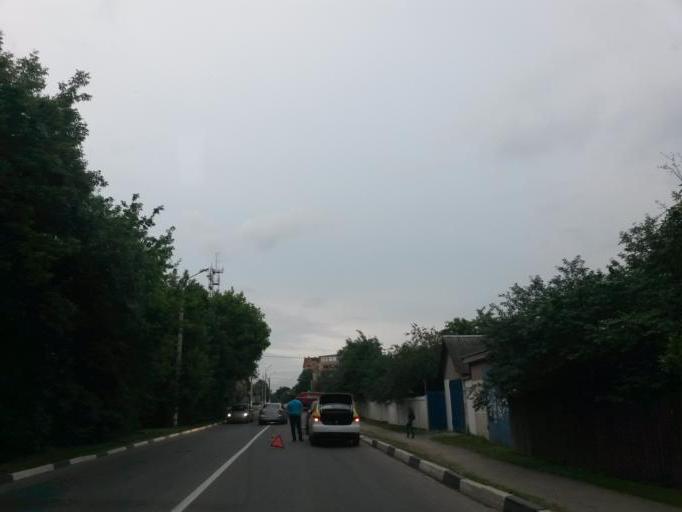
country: RU
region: Moskovskaya
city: Domodedovo
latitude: 55.4316
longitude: 37.7619
